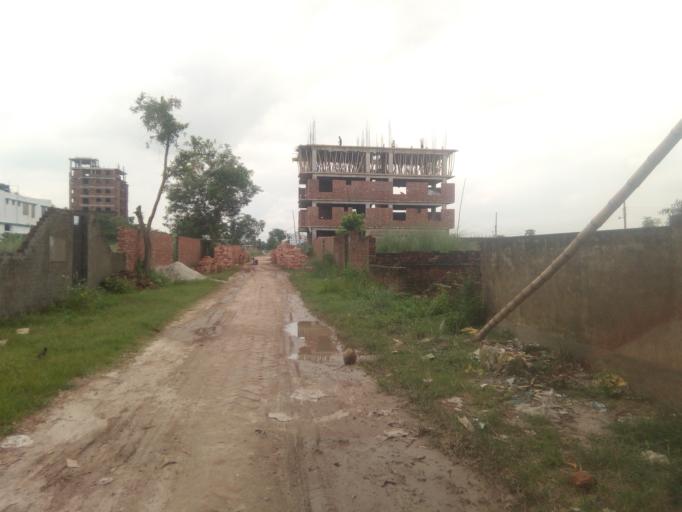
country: BD
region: Dhaka
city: Azimpur
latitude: 23.7545
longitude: 90.3488
